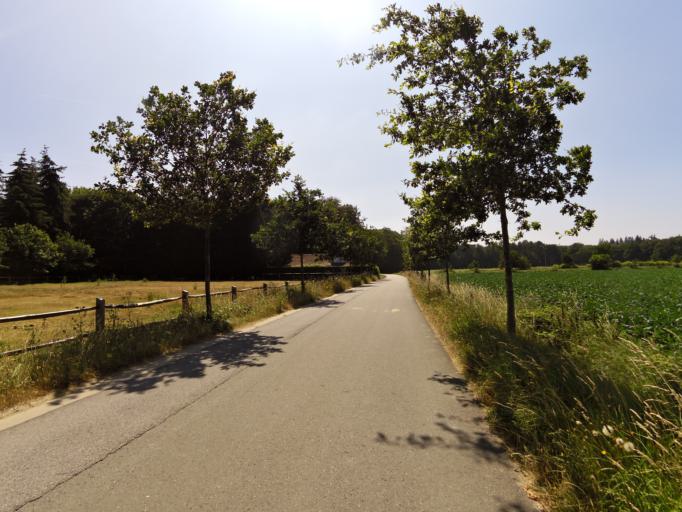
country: BE
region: Flanders
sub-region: Provincie West-Vlaanderen
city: Zedelgem
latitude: 51.1778
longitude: 3.1715
